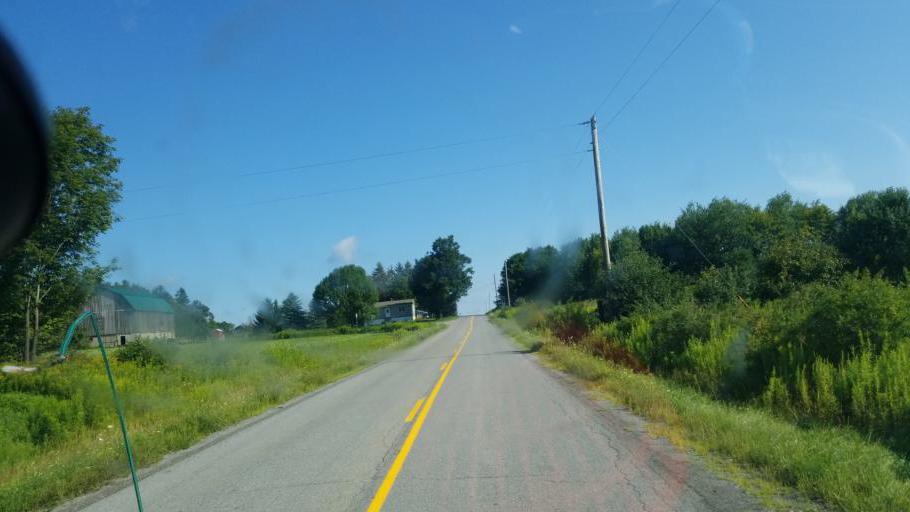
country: US
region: New York
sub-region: Allegany County
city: Andover
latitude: 42.1676
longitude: -77.7131
